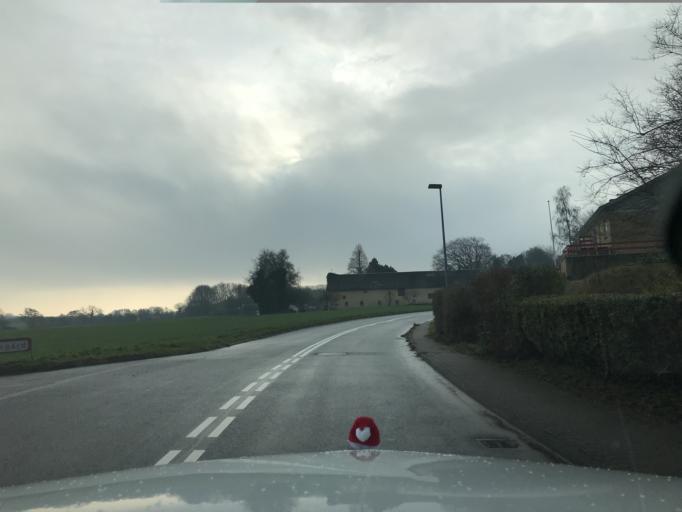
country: DK
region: South Denmark
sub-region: Sonderborg Kommune
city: Grasten
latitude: 54.8944
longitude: 9.5641
